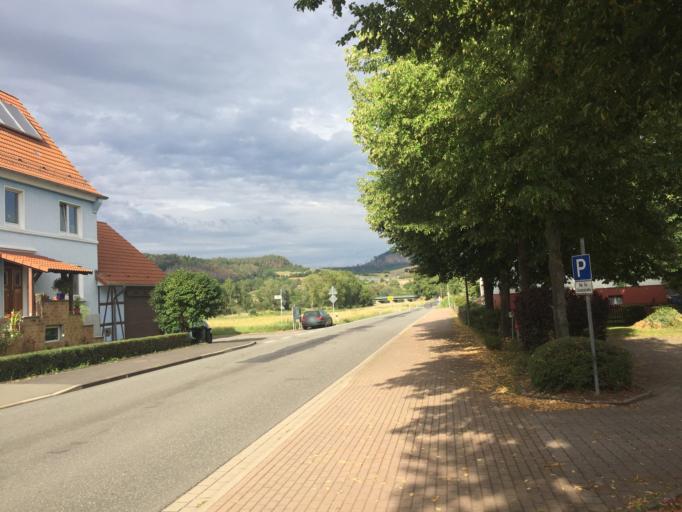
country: DE
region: Hesse
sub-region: Regierungsbezirk Kassel
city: Alheim
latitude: 51.0260
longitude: 9.6739
